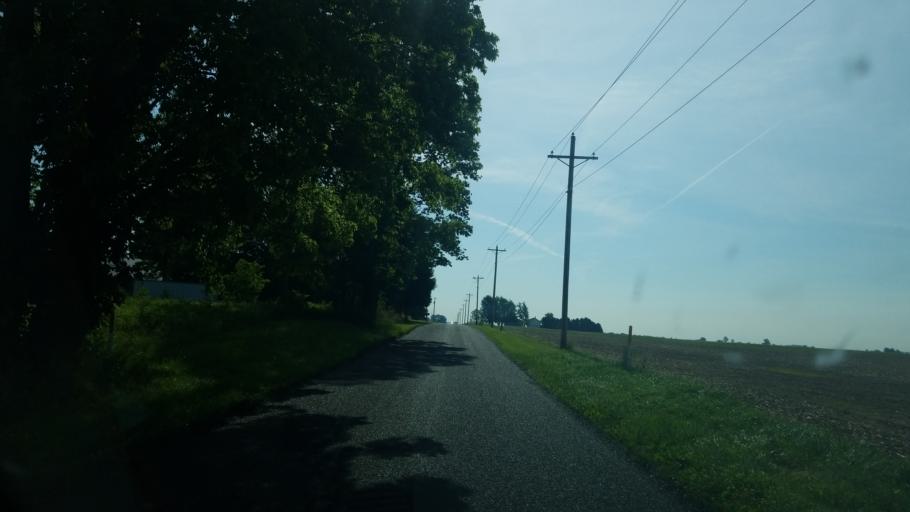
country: US
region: Ohio
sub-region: Hancock County
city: Findlay
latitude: 41.0215
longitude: -83.5541
